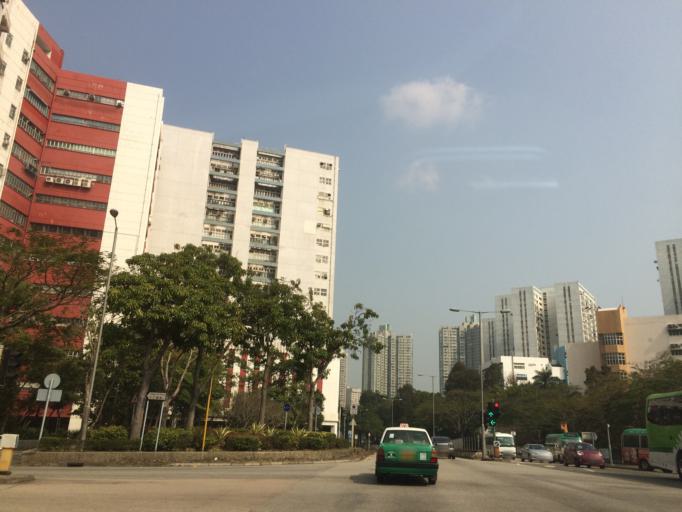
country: HK
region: Tai Po
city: Tai Po
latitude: 22.4553
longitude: 114.1654
